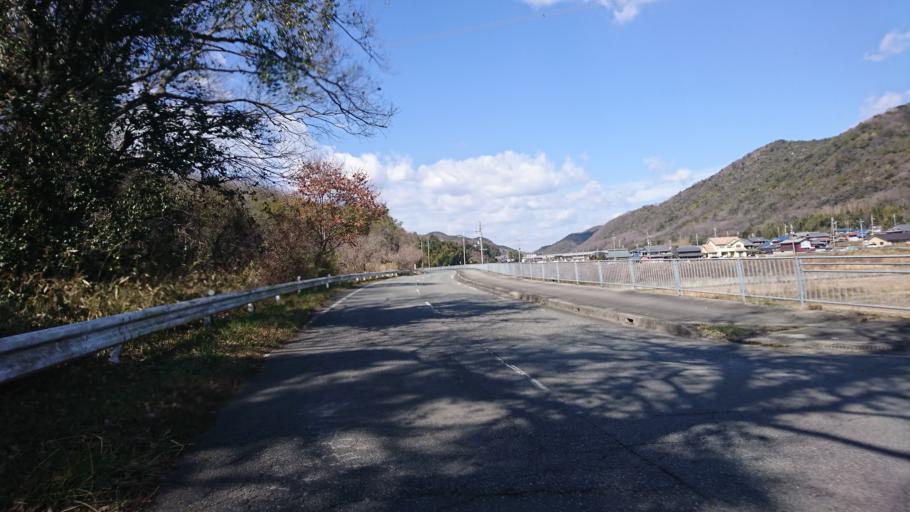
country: JP
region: Hyogo
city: Kakogawacho-honmachi
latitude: 34.8415
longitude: 134.8179
